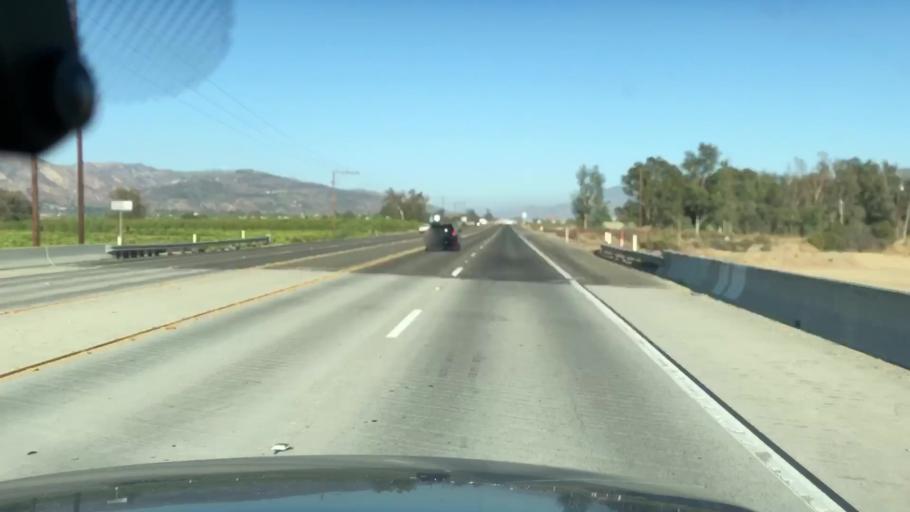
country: US
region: California
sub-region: Ventura County
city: Fillmore
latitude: 34.3935
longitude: -118.9481
